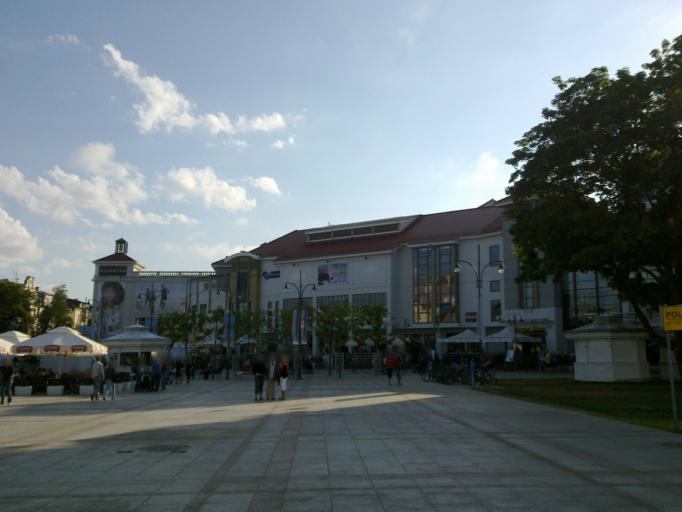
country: PL
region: Pomeranian Voivodeship
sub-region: Sopot
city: Sopot
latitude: 54.4452
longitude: 18.5687
